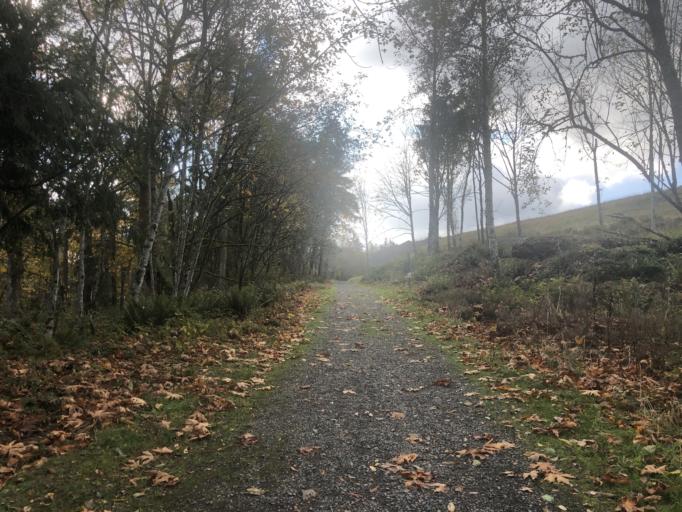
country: US
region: Washington
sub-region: Thurston County
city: Tanglewilde-Thompson Place
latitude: 47.1129
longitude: -122.7559
